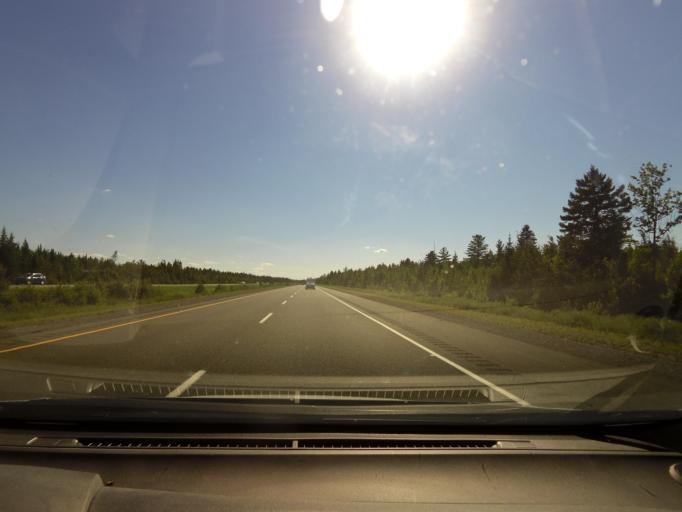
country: CA
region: Quebec
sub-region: Mauricie
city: Becancour
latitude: 46.4940
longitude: -72.3108
